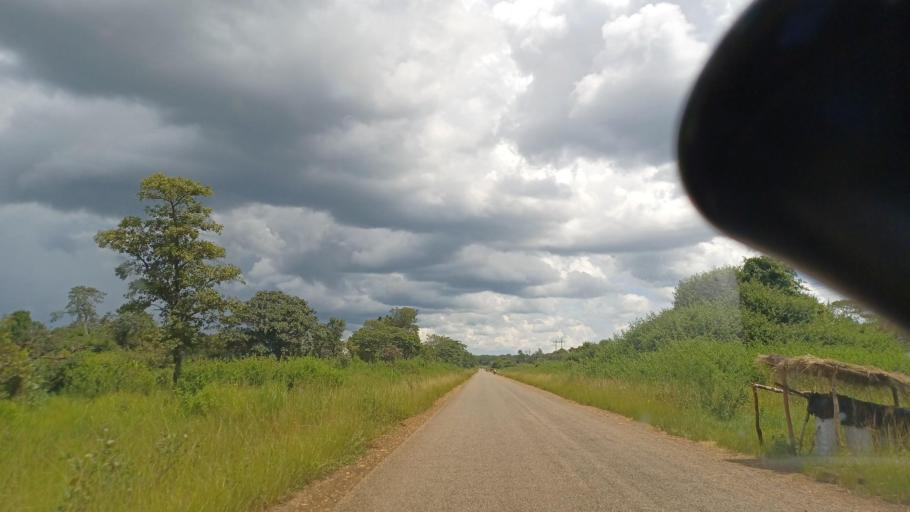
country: ZM
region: North-Western
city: Kasempa
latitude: -12.7725
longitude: 26.0137
